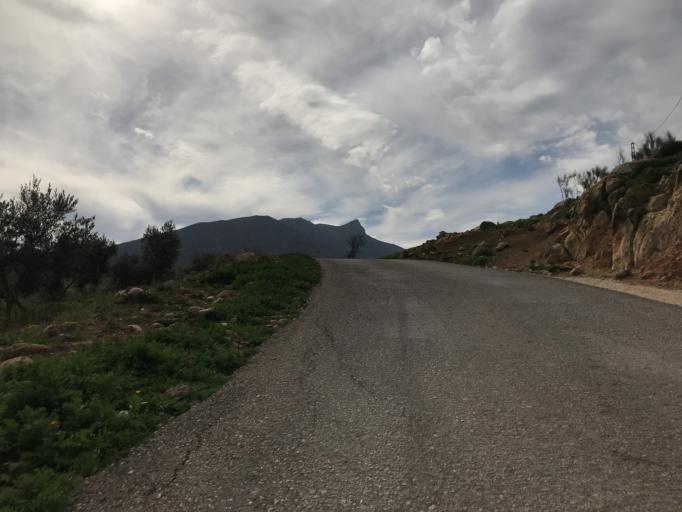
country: ES
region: Andalusia
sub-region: Provincia de Malaga
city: Ardales
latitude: 36.8831
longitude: -4.8579
